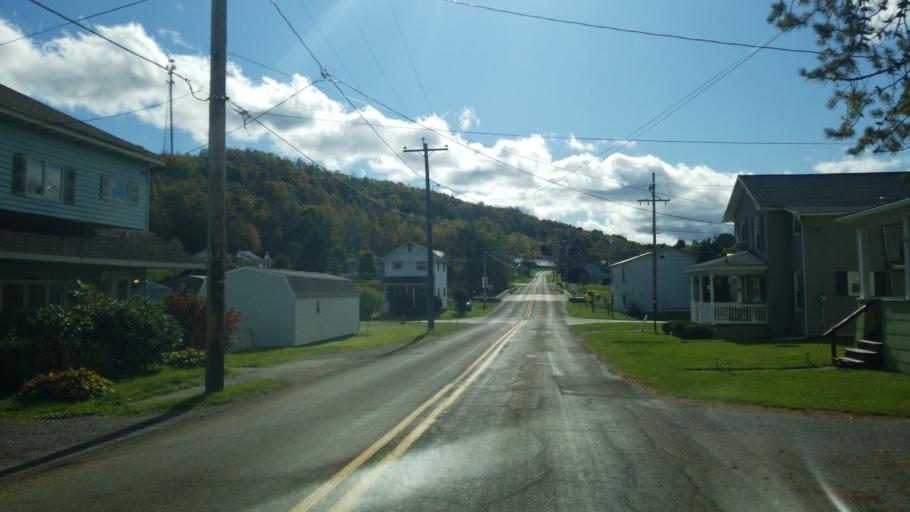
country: US
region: Pennsylvania
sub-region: Jefferson County
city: Reynoldsville
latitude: 41.0890
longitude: -78.8832
